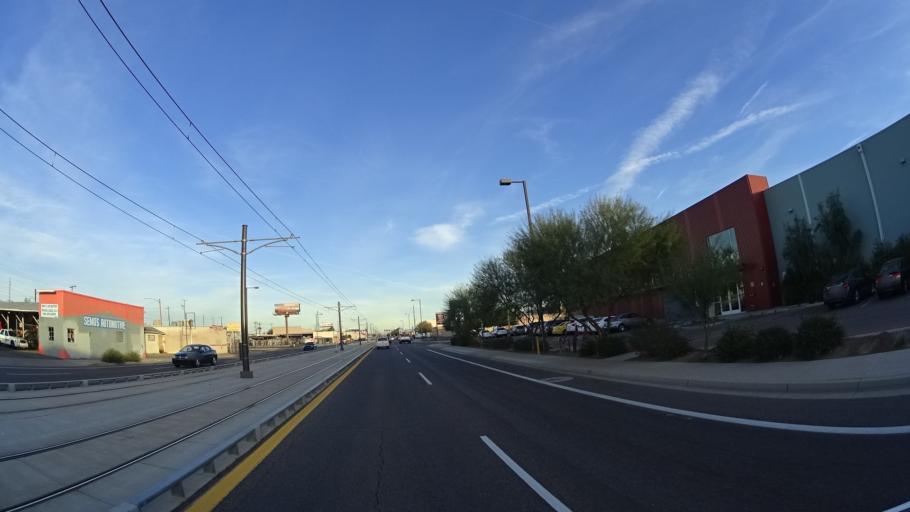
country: US
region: Arizona
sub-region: Maricopa County
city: Phoenix
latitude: 33.4482
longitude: -112.0205
